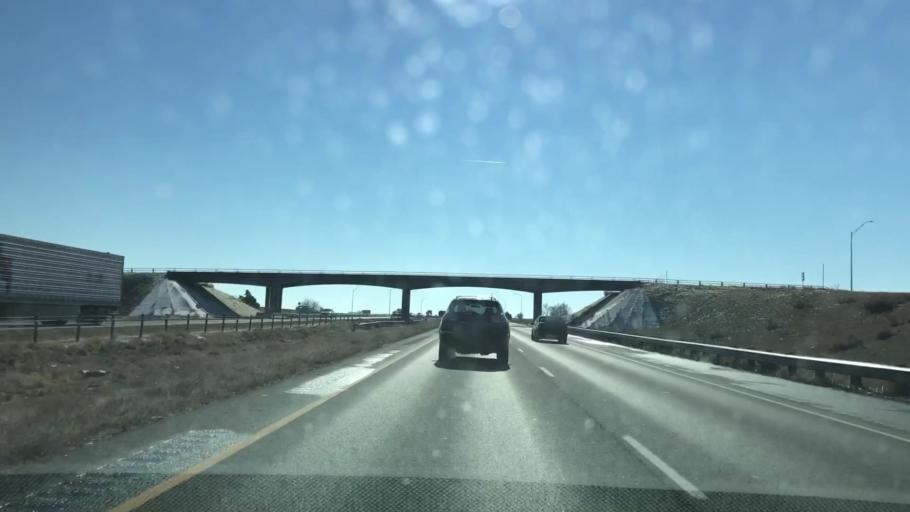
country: US
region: Colorado
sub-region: Weld County
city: Mead
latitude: 40.2345
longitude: -104.9803
